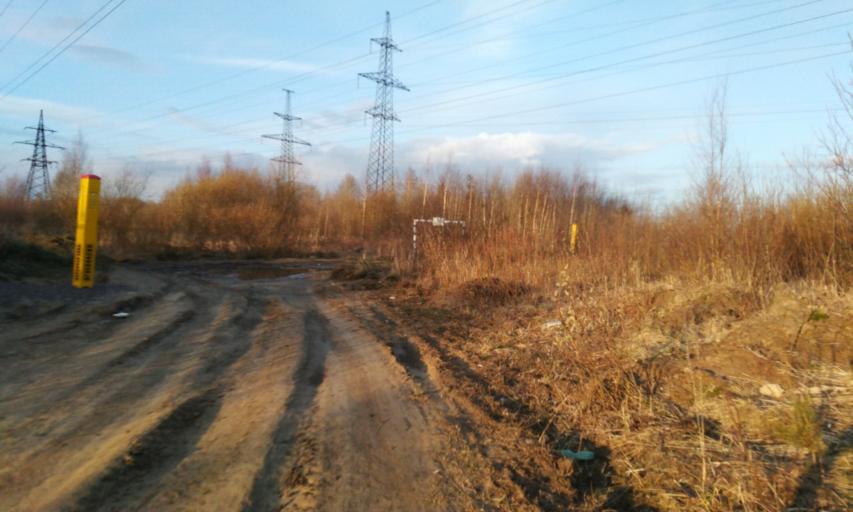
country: RU
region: Leningrad
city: Novoye Devyatkino
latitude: 60.0839
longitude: 30.4618
